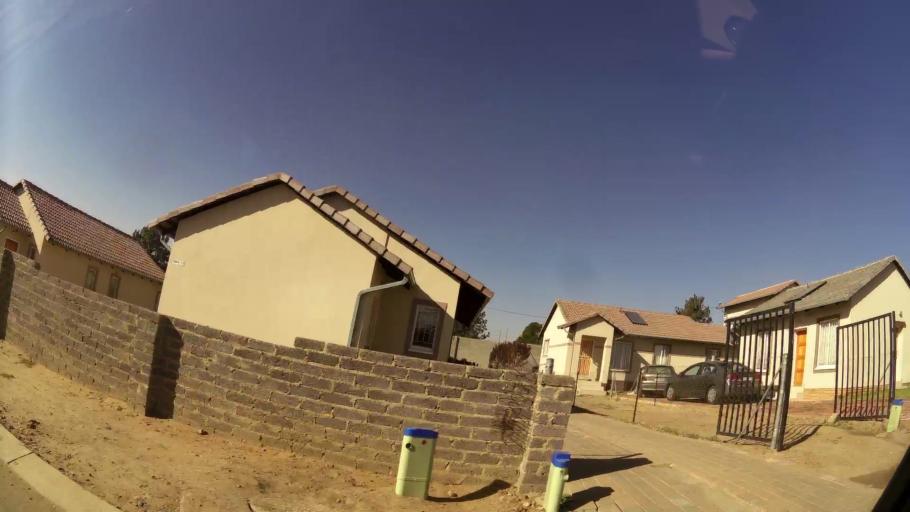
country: ZA
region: Gauteng
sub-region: City of Johannesburg Metropolitan Municipality
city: Diepsloot
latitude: -26.0200
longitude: 27.9673
